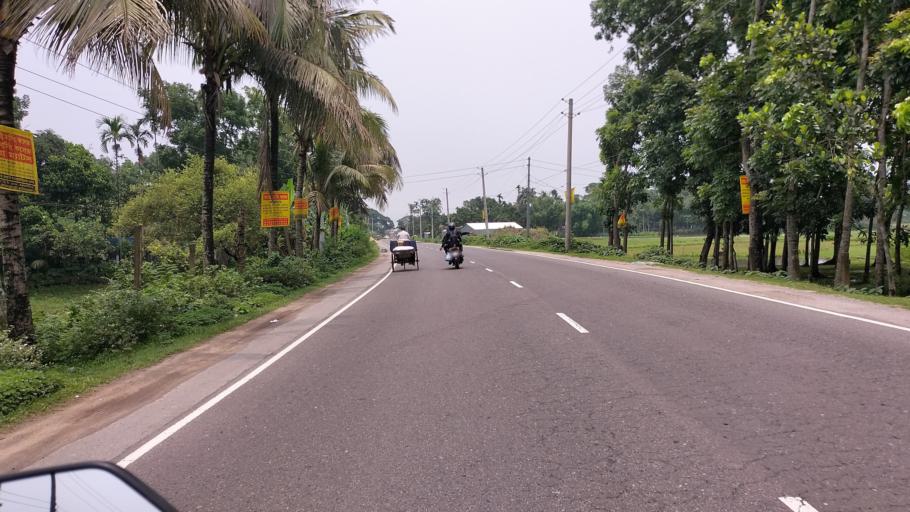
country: BD
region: Dhaka
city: Mymensingh
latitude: 24.7763
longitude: 90.4677
